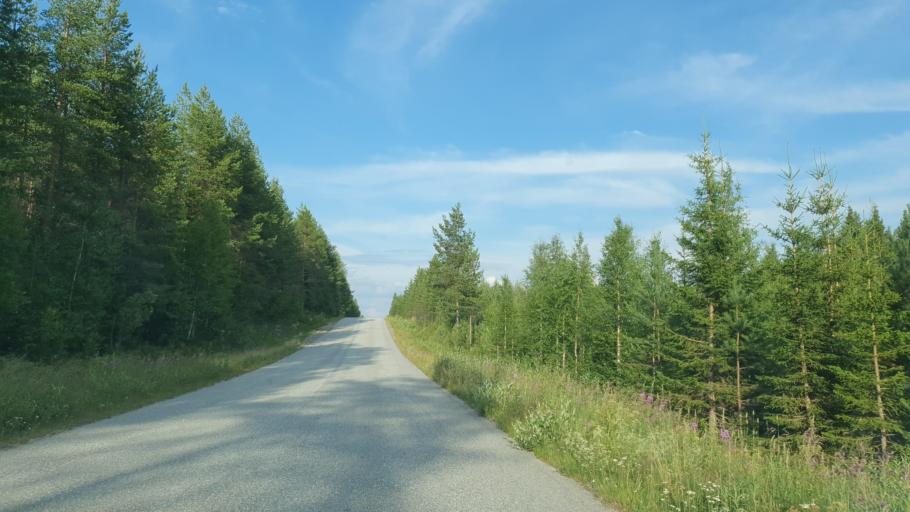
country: FI
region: Kainuu
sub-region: Kehys-Kainuu
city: Kuhmo
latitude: 64.3143
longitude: 29.5141
